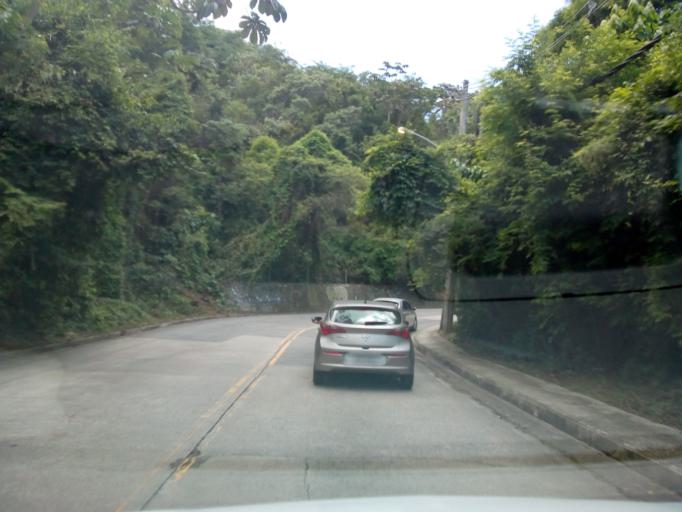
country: BR
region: Rio de Janeiro
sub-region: Rio De Janeiro
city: Rio de Janeiro
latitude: -22.9824
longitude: -43.2983
